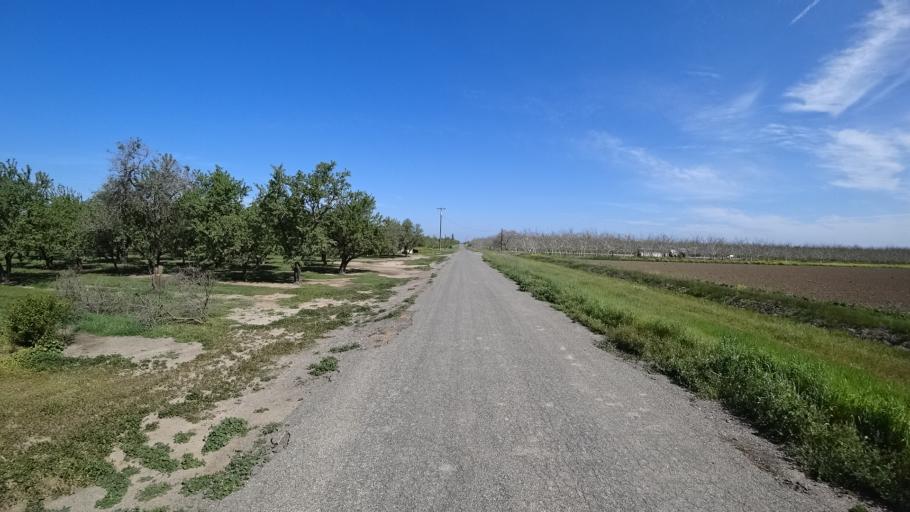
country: US
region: California
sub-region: Glenn County
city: Hamilton City
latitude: 39.6261
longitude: -122.0181
